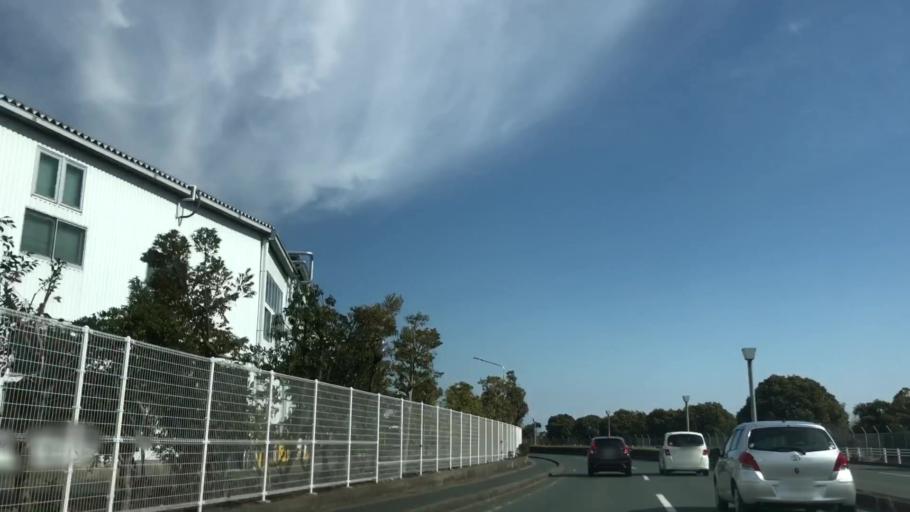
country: JP
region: Shizuoka
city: Hamamatsu
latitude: 34.7525
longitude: 137.7172
